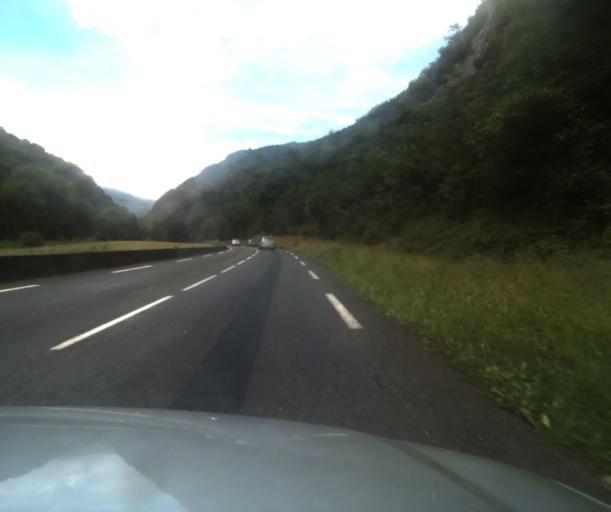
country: FR
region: Midi-Pyrenees
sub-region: Departement des Hautes-Pyrenees
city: Pierrefitte-Nestalas
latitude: 42.9436
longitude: -0.0534
